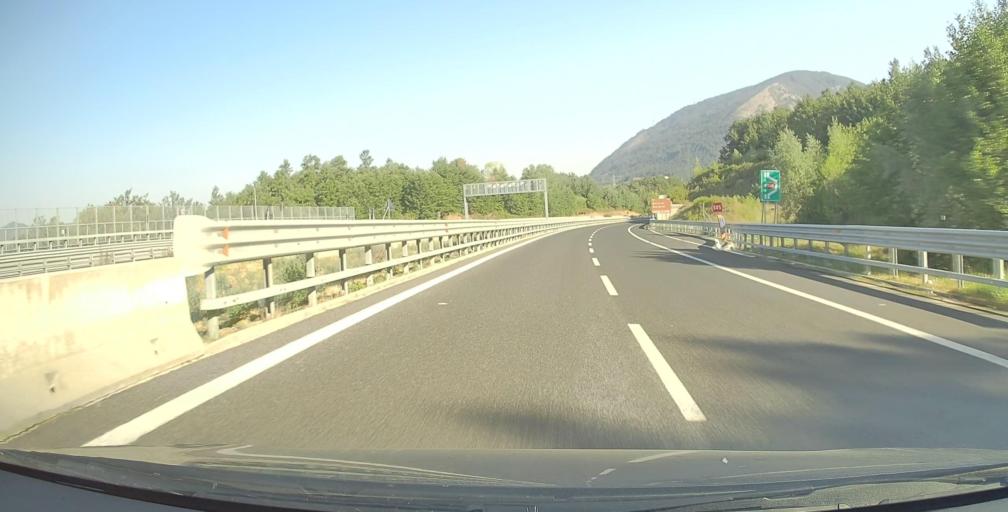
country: IT
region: Basilicate
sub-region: Provincia di Potenza
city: Lagonegro
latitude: 40.1146
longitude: 15.7862
